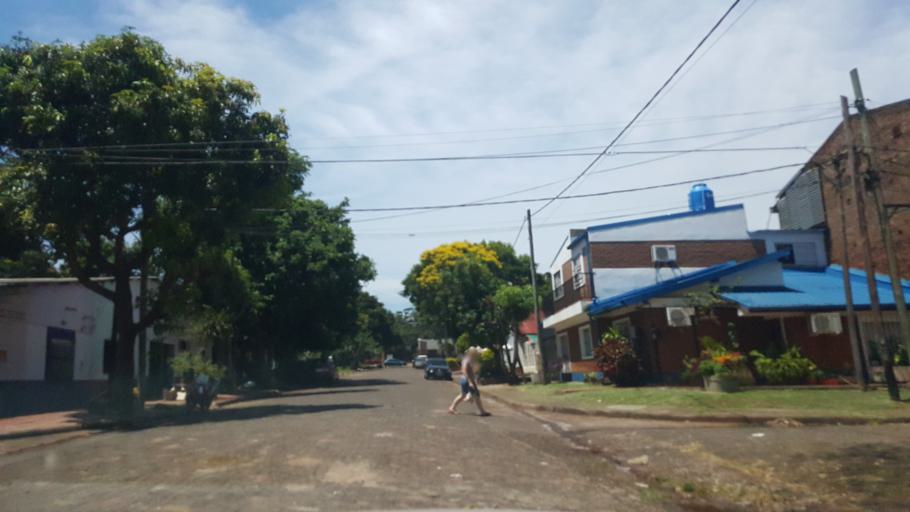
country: AR
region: Misiones
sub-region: Departamento de Capital
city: Posadas
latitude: -27.3969
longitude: -55.8996
